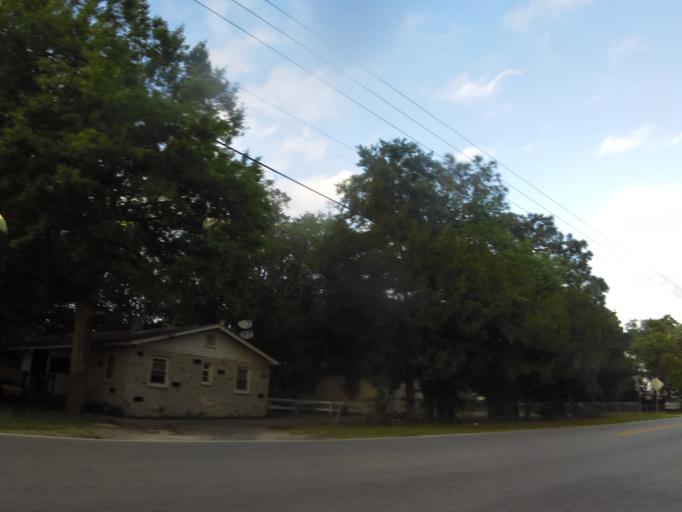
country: US
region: Florida
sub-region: Duval County
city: Jacksonville
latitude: 30.4470
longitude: -81.6298
